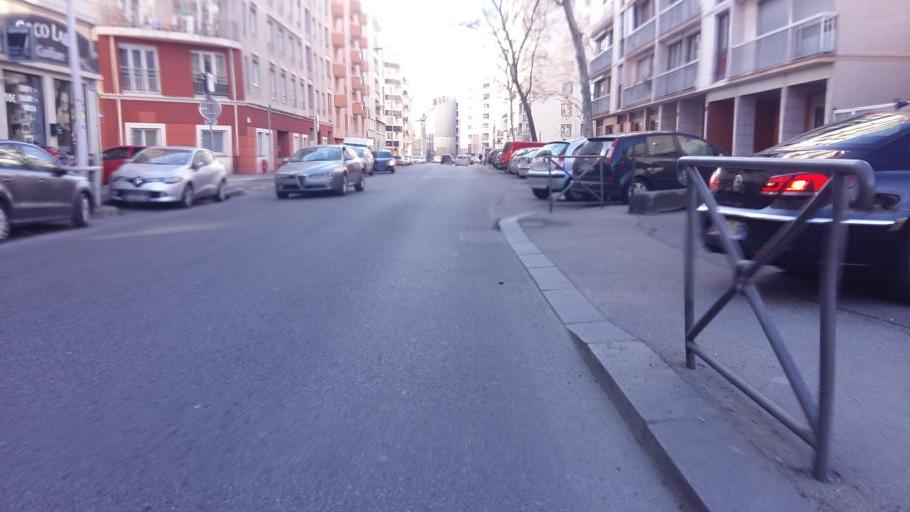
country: FR
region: Rhone-Alpes
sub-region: Departement du Rhone
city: Villeurbanne
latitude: 45.7547
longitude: 4.8810
